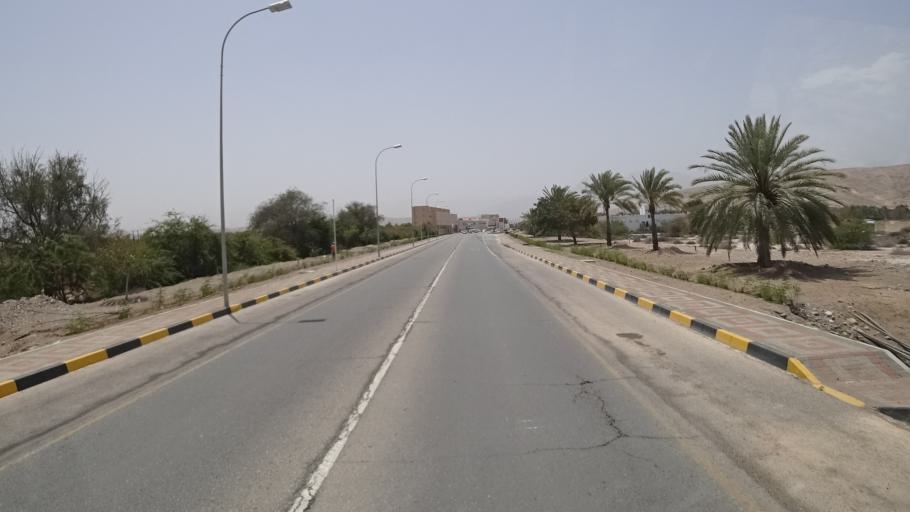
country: OM
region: Muhafazat Masqat
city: Muscat
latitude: 23.2451
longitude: 58.9043
